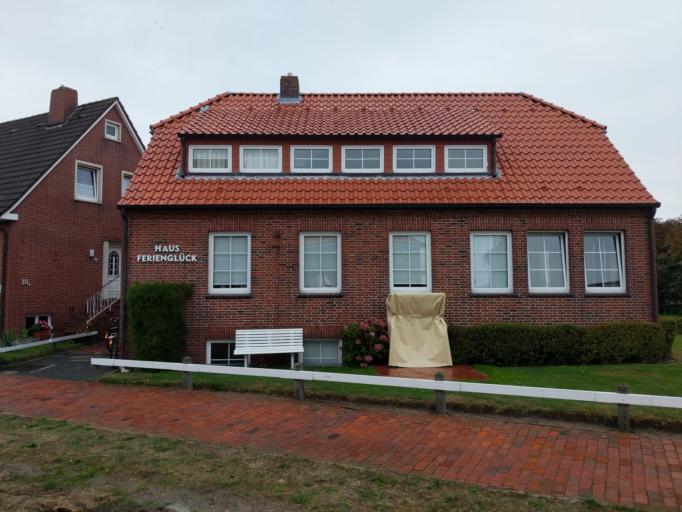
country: DE
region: Lower Saxony
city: Juist
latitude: 53.6769
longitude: 7.0031
